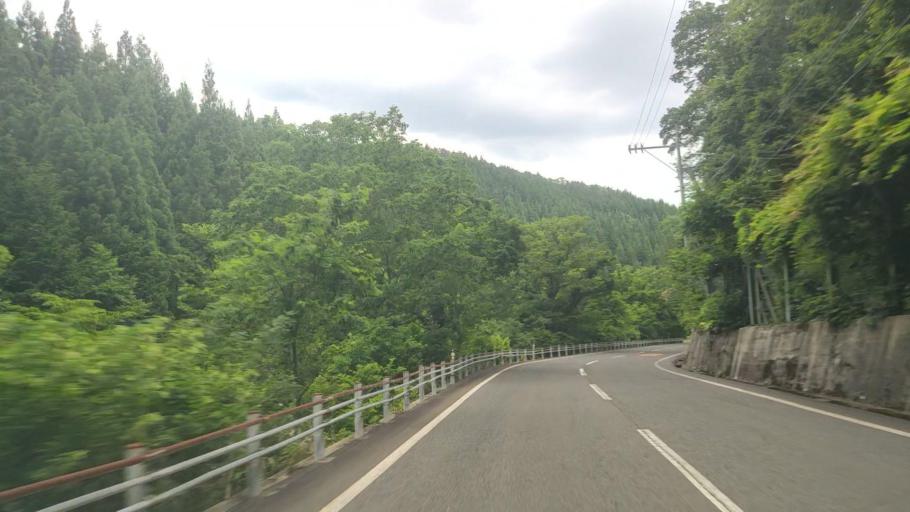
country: JP
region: Tottori
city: Kurayoshi
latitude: 35.2933
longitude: 133.9872
